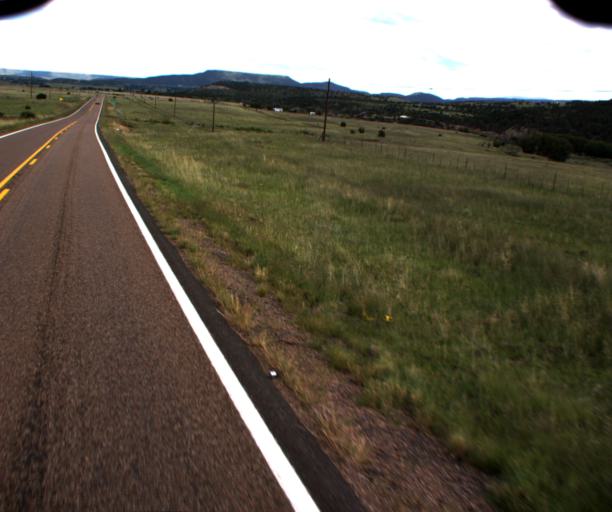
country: US
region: Arizona
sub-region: Apache County
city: Eagar
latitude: 34.1041
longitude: -109.3602
